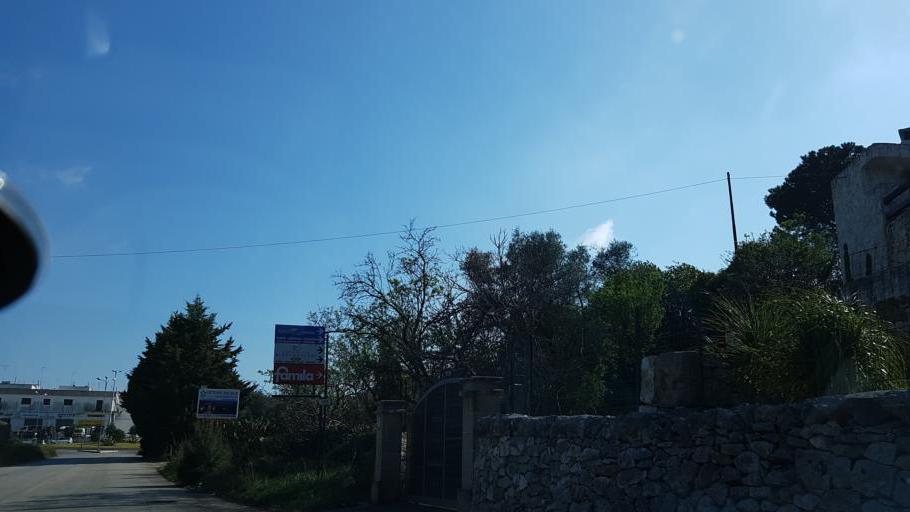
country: IT
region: Apulia
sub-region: Provincia di Brindisi
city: Ostuni
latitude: 40.7254
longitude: 17.5911
